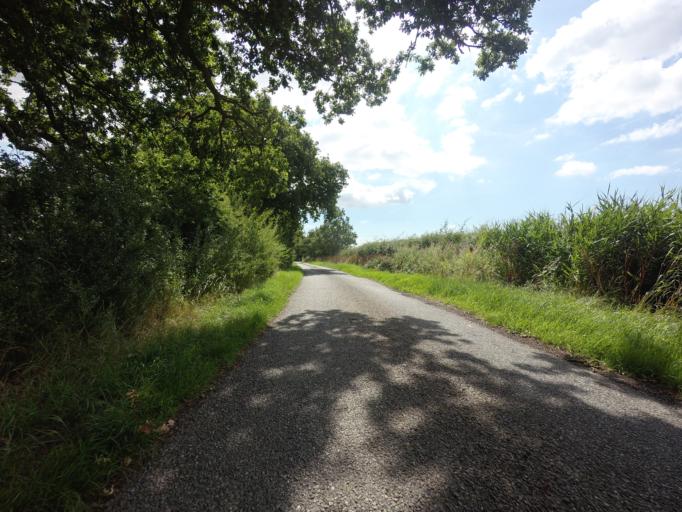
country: GB
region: England
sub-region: Kent
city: Stone
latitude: 51.0487
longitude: 0.7727
